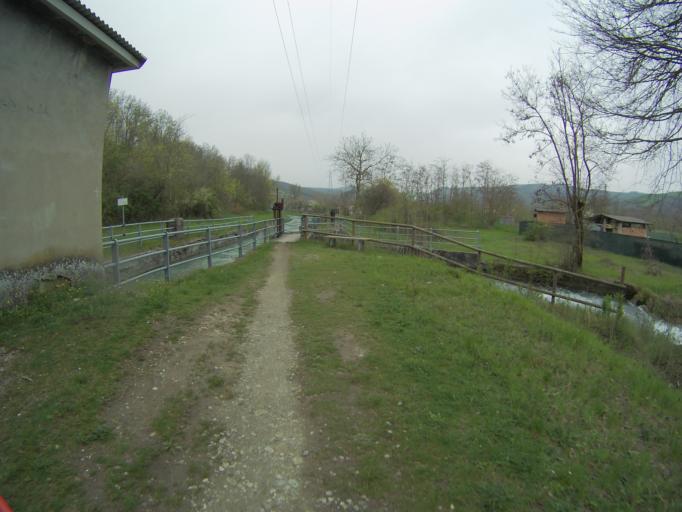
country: IT
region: Emilia-Romagna
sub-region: Provincia di Reggio Emilia
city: Ciano d'Enza
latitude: 44.6009
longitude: 10.4047
